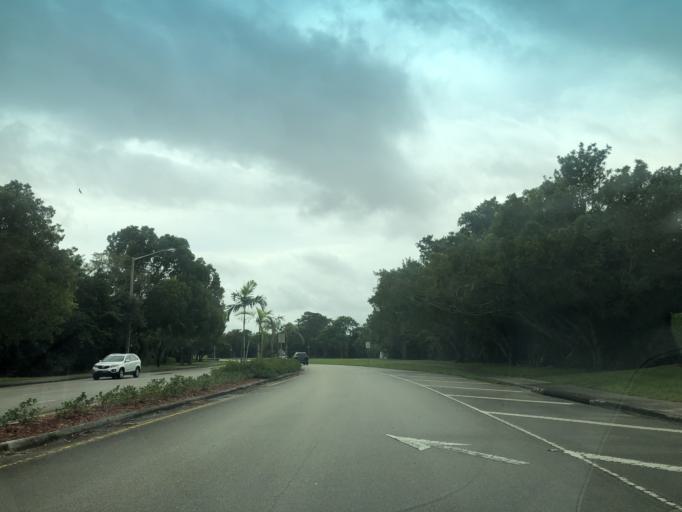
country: US
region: Florida
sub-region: Broward County
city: North Lauderdale
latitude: 26.2349
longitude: -80.2378
